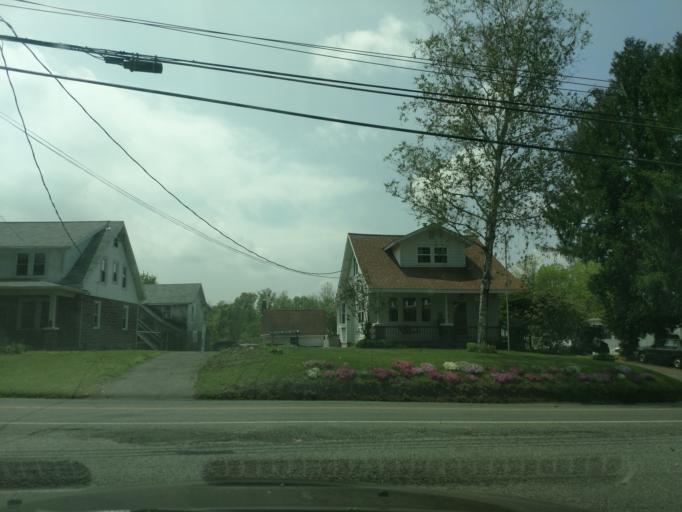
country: US
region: Pennsylvania
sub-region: Chester County
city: Elverson
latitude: 40.2059
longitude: -75.8369
